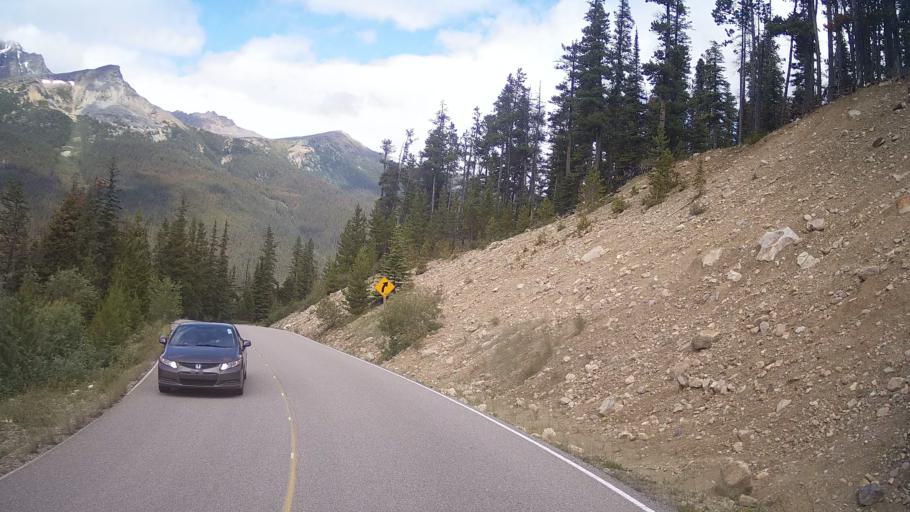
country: CA
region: Alberta
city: Jasper Park Lodge
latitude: 52.7141
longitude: -118.0550
